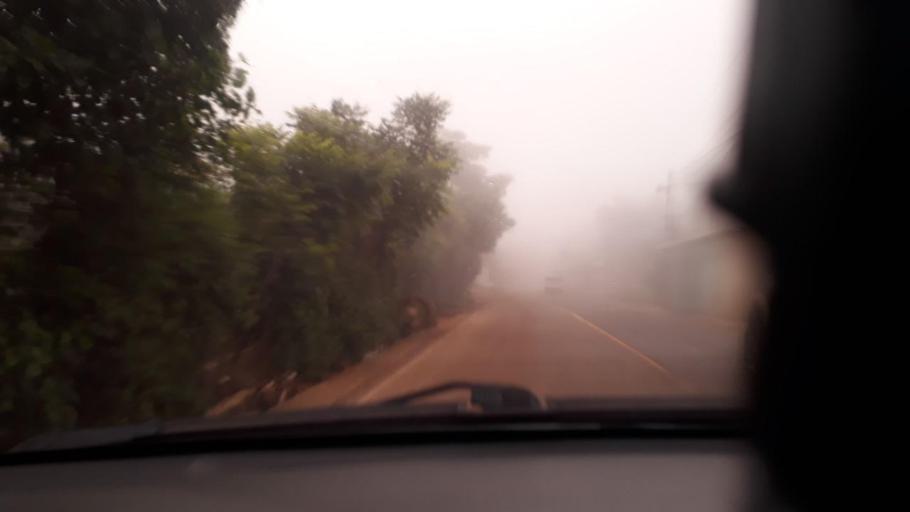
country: GT
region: Jutiapa
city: Jalpatagua
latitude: 14.1818
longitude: -90.0216
